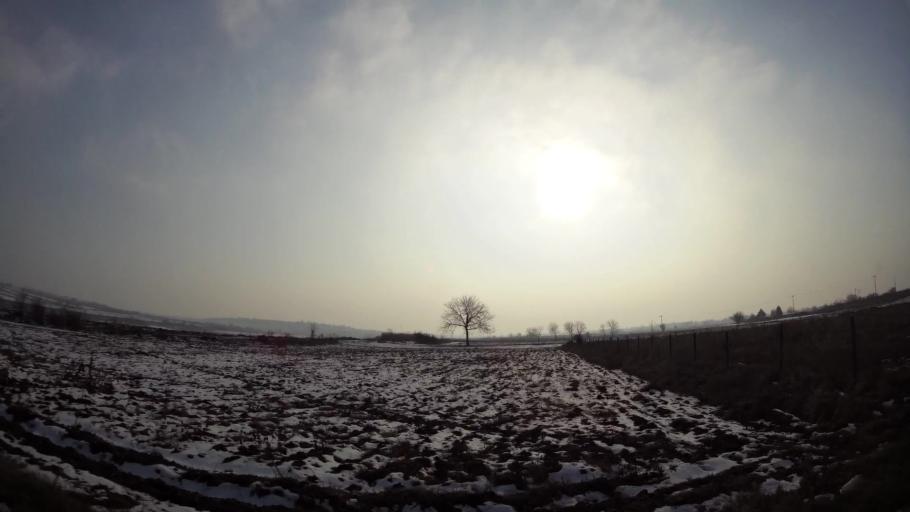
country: MK
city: Miladinovci
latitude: 41.9742
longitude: 21.6422
